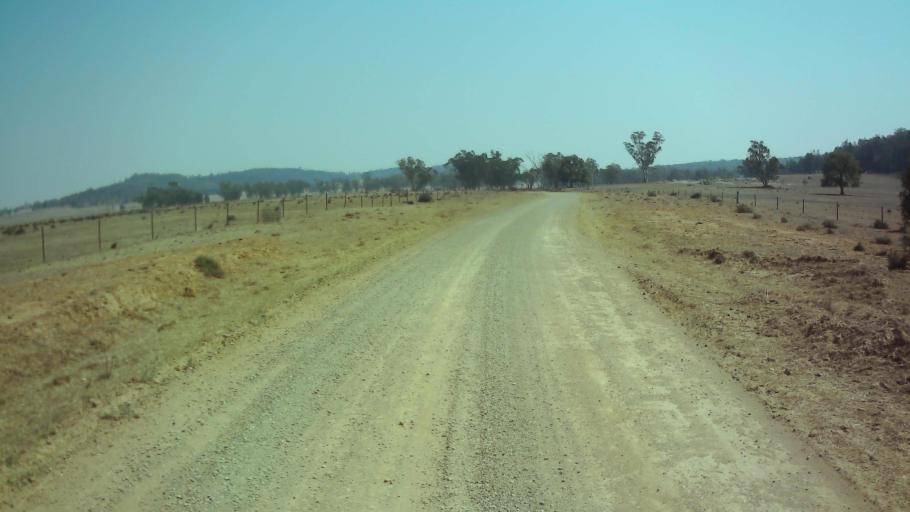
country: AU
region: New South Wales
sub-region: Weddin
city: Grenfell
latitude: -33.6795
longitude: 148.2772
